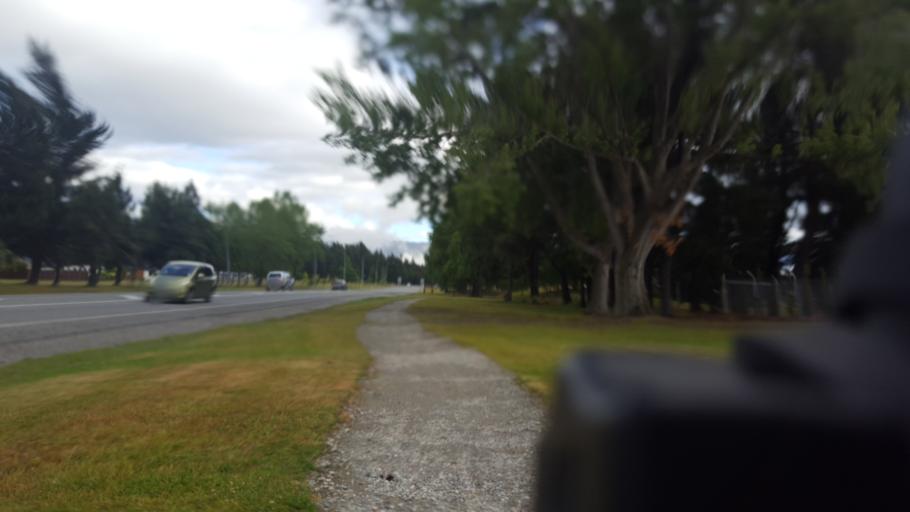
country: NZ
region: Otago
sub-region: Queenstown-Lakes District
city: Wanaka
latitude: -45.2433
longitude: 169.3784
